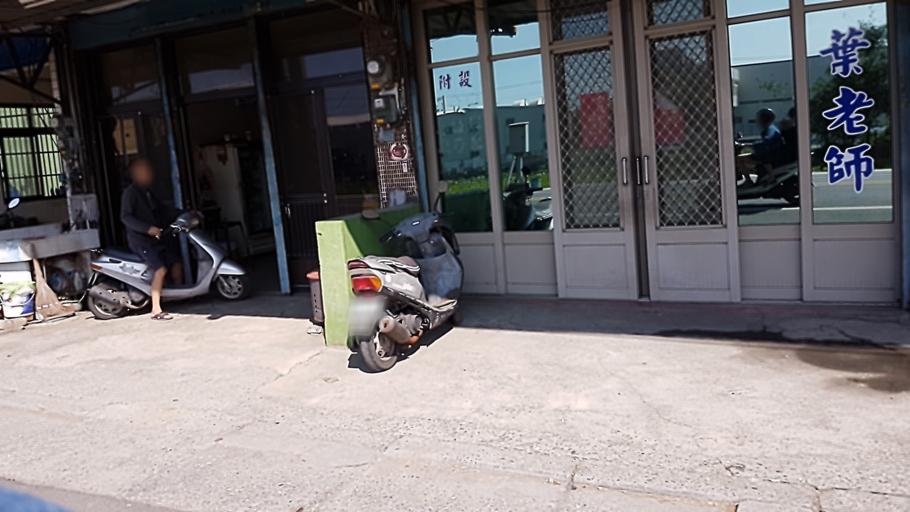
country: TW
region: Taiwan
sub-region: Changhua
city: Chang-hua
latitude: 24.0835
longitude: 120.4864
